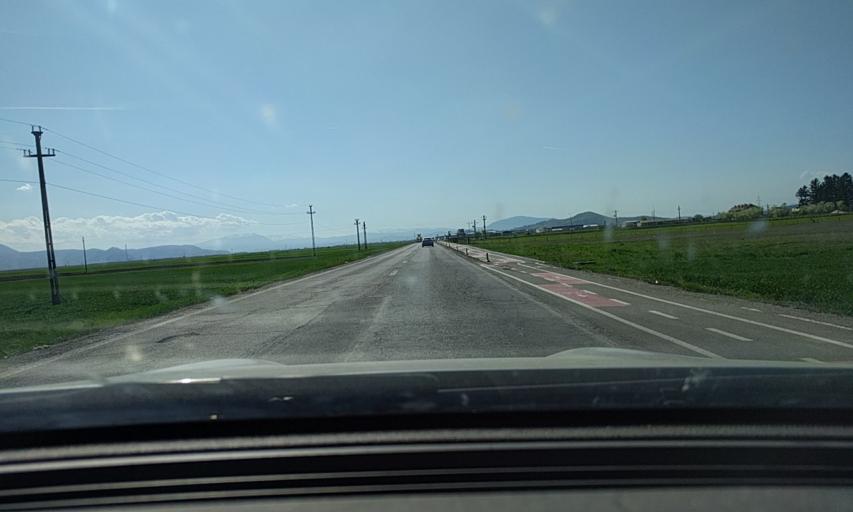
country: RO
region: Brasov
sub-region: Comuna Prejmer
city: Prejmer
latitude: 45.7175
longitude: 25.7618
